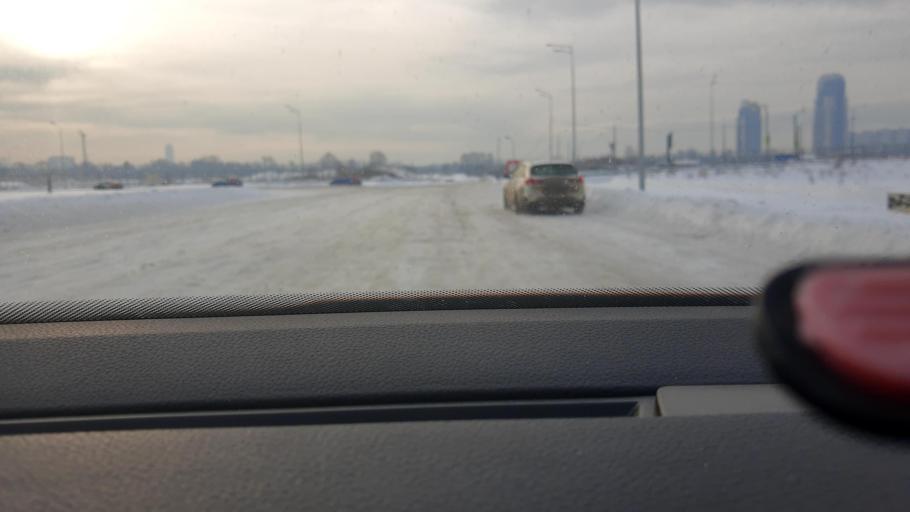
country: RU
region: Moscow
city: Strogino
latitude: 55.8153
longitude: 37.4339
